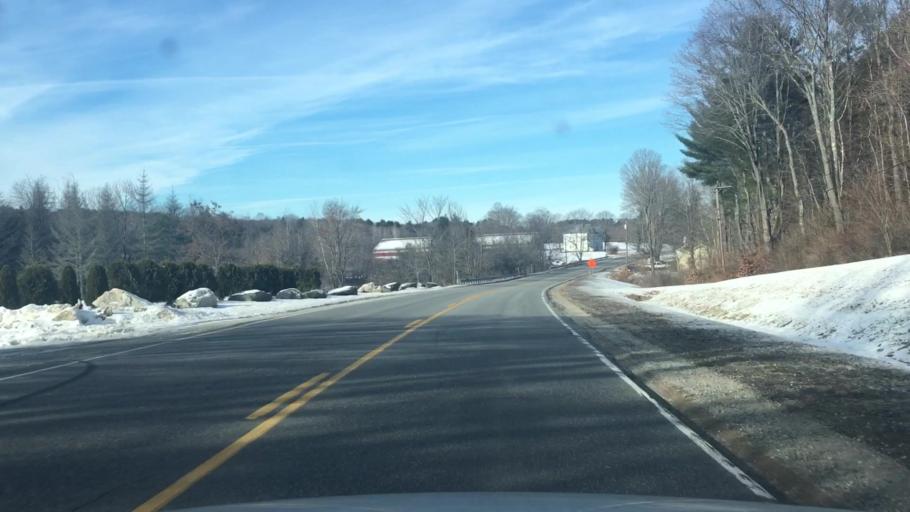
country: US
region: Maine
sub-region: Androscoggin County
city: Lewiston
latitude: 44.0559
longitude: -70.2046
